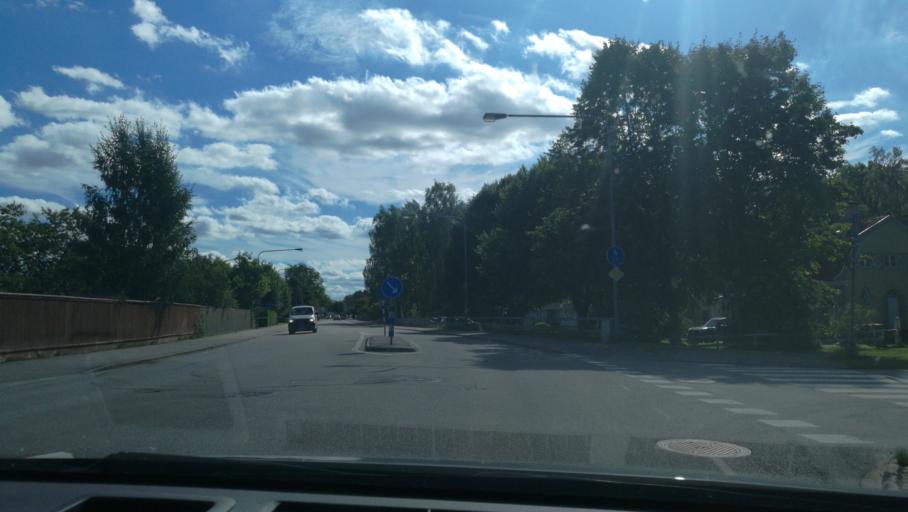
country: SE
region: Vaestra Goetaland
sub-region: Mariestads Kommun
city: Mariestad
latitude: 58.6992
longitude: 13.8366
